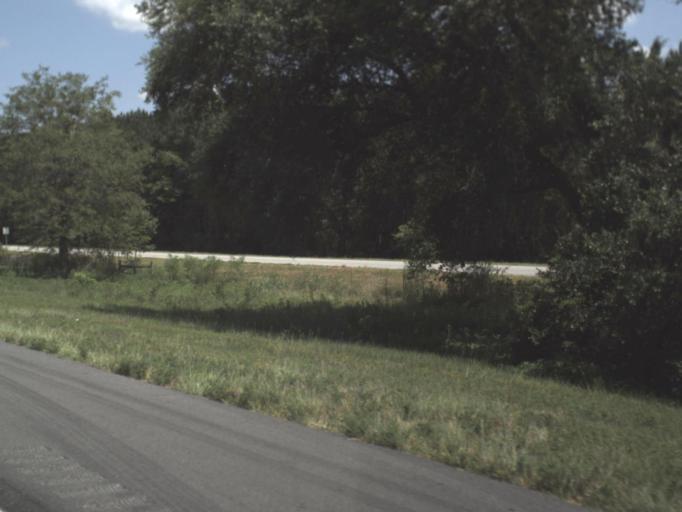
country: US
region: Florida
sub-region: Madison County
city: Madison
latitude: 30.3927
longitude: -83.3412
